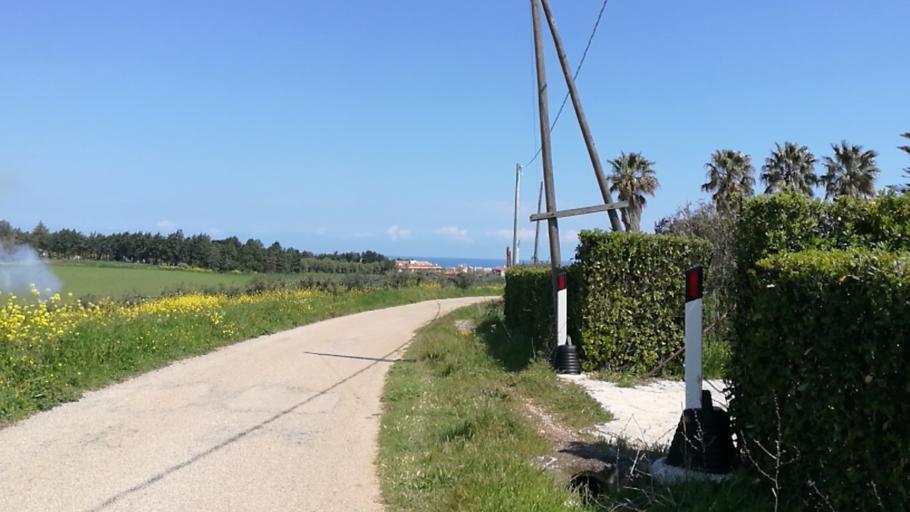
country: IT
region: Molise
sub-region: Provincia di Campobasso
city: Termoli
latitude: 41.9731
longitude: 14.9833
